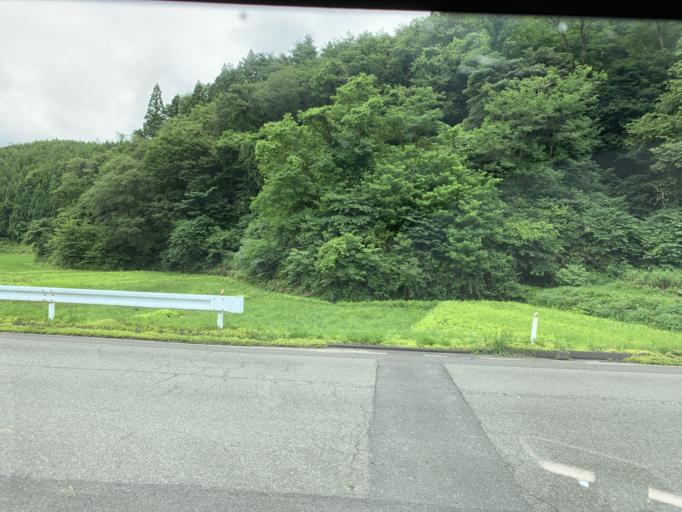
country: JP
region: Iwate
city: Ichinoseki
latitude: 38.8984
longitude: 140.9783
